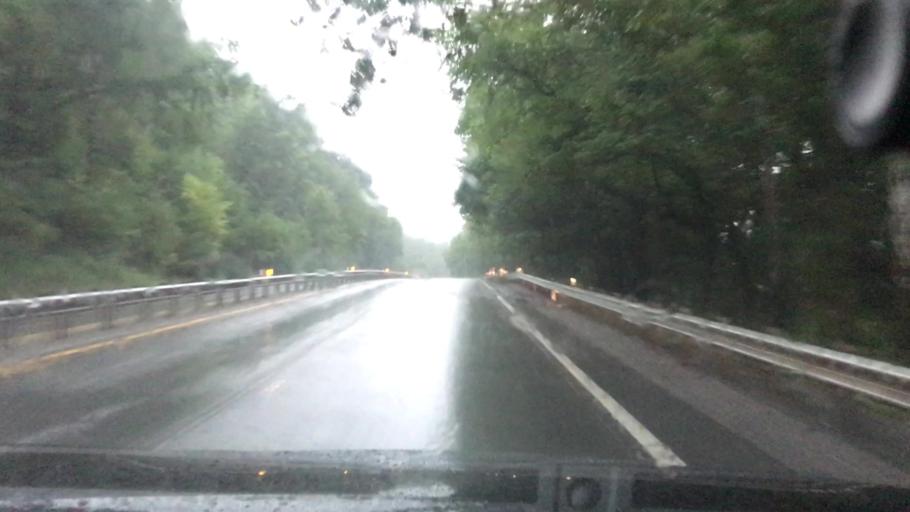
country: US
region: Virginia
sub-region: Giles County
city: Narrows
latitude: 37.3464
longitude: -80.7828
